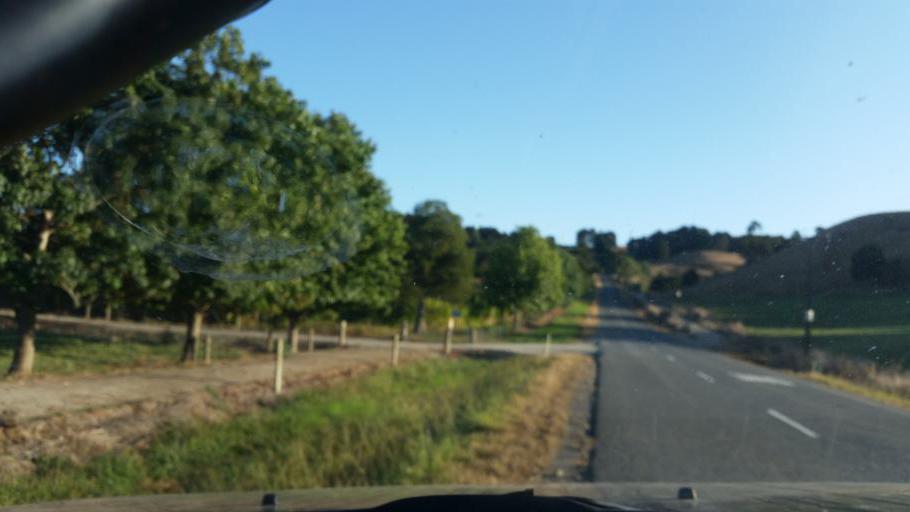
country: NZ
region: Northland
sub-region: Kaipara District
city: Dargaville
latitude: -35.8471
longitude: 174.0309
